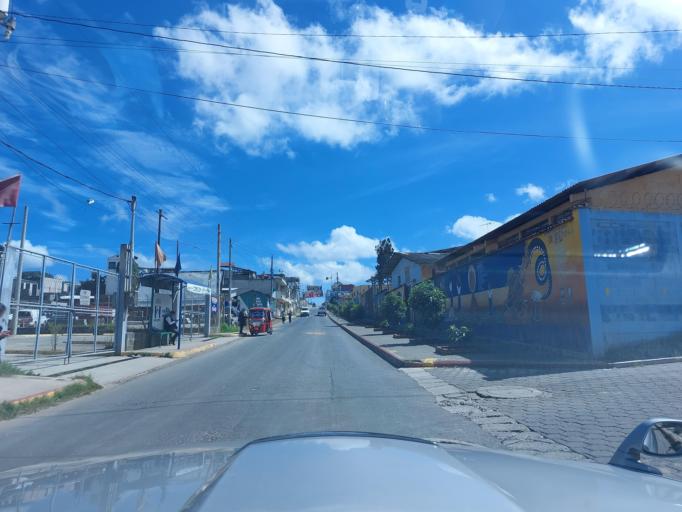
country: GT
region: Chimaltenango
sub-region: Municipio de San Juan Comalapa
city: Comalapa
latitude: 14.7309
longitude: -90.8871
